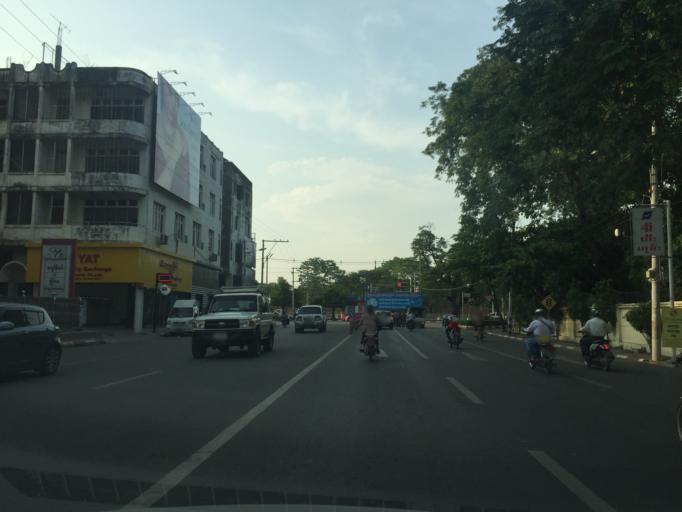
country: MM
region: Mandalay
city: Mandalay
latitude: 21.9822
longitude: 96.0872
